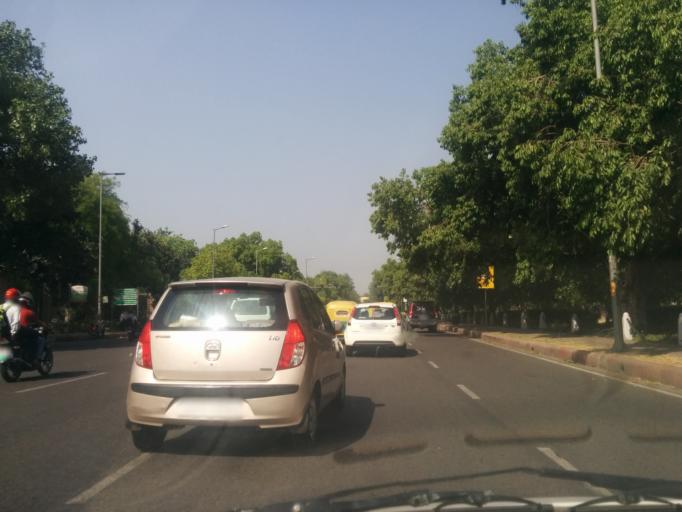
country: IN
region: NCT
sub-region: New Delhi
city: New Delhi
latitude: 28.6107
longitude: 77.2337
